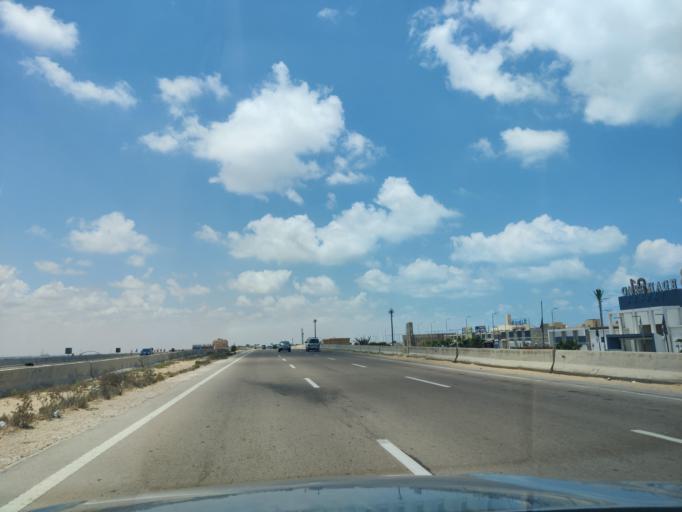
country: EG
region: Muhafazat Matruh
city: Al `Alamayn
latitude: 30.8254
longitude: 29.1934
